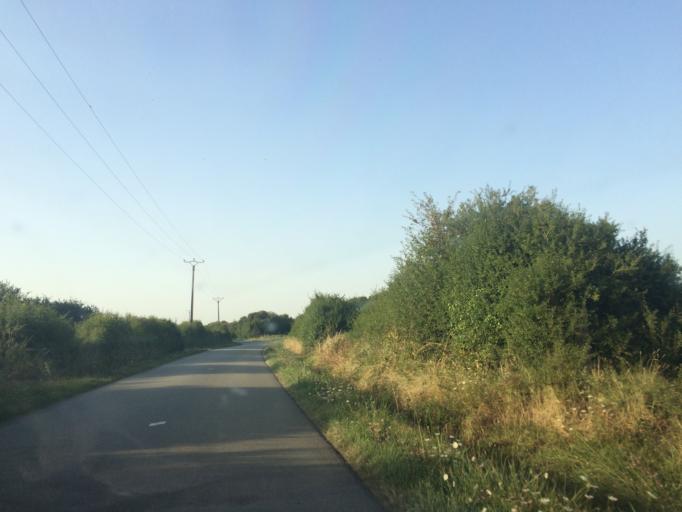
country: FR
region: Brittany
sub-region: Departement du Morbihan
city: Damgan
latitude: 47.5199
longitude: -2.5553
